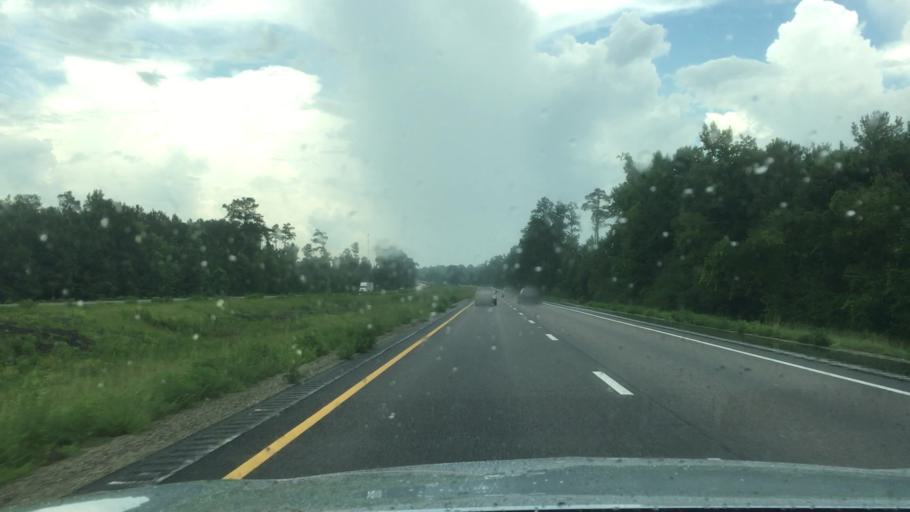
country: US
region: Mississippi
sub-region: Lamar County
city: Purvis
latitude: 31.1714
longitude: -89.3505
